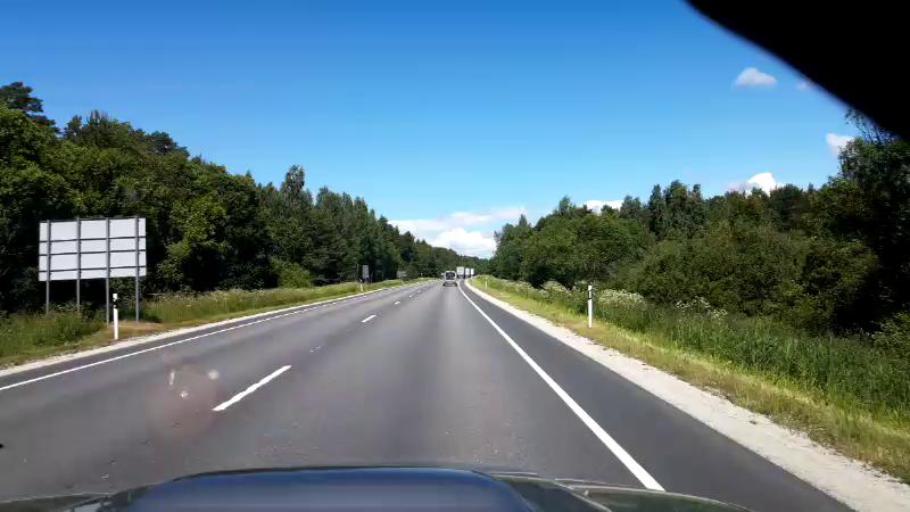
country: LV
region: Salacgrivas
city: Ainazi
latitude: 58.0910
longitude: 24.5079
